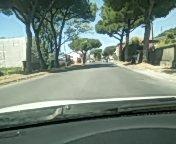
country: IT
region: Tuscany
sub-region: Provincia di Massa-Carrara
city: Massa
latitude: 44.0410
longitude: 10.0917
